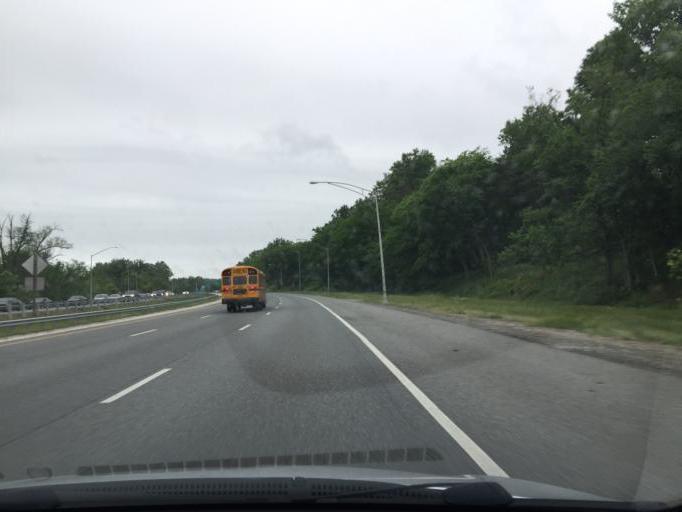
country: US
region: Maryland
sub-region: Baltimore County
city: Mays Chapel
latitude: 39.4031
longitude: -76.6618
